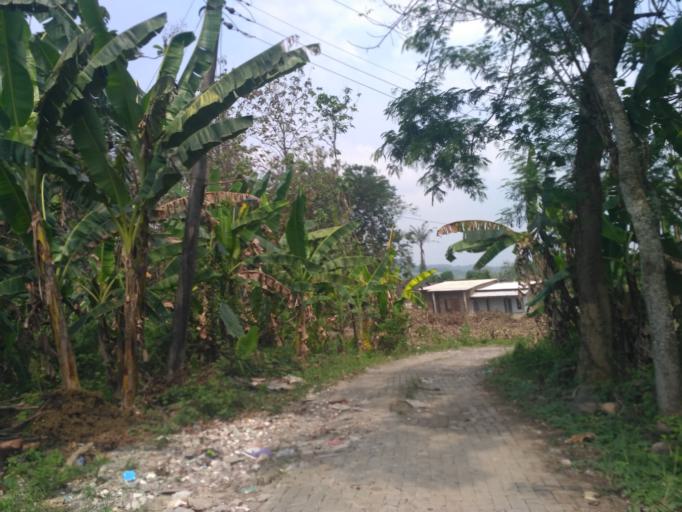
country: ID
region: Central Java
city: Mranggen
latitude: -7.0657
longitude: 110.4655
